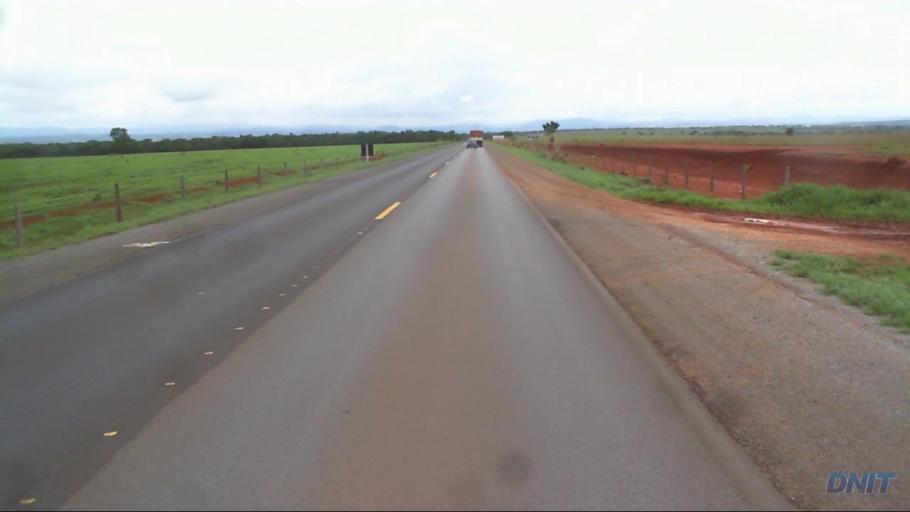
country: BR
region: Goias
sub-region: Padre Bernardo
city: Padre Bernardo
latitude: -15.1695
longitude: -48.3660
